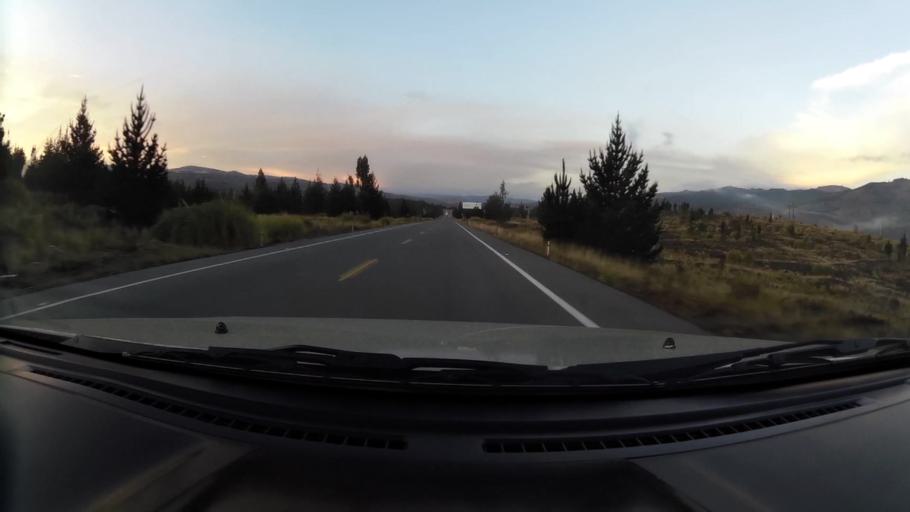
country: EC
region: Chimborazo
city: Alausi
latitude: -2.0368
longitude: -78.7366
